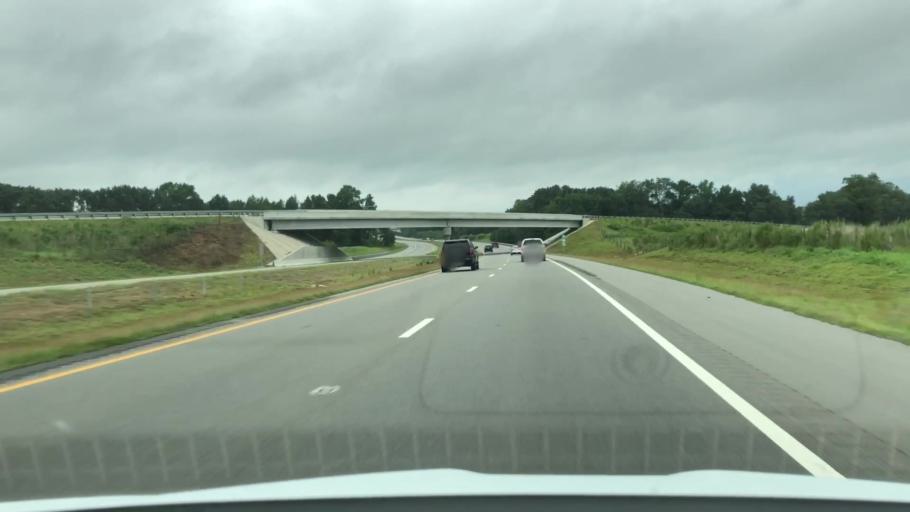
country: US
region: North Carolina
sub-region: Wayne County
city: Elroy
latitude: 35.3543
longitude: -77.8484
